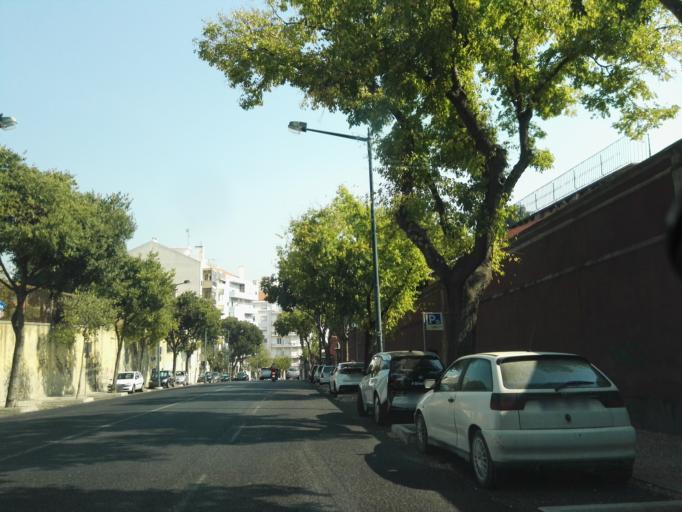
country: PT
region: Lisbon
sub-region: Lisbon
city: Lisbon
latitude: 38.7275
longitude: -9.1392
